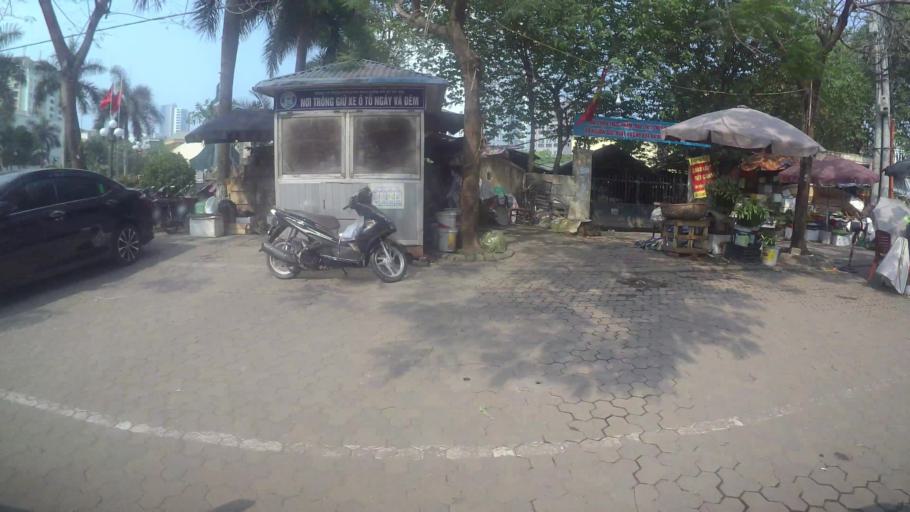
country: VN
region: Ha Noi
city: Tay Ho
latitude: 21.0635
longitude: 105.8071
